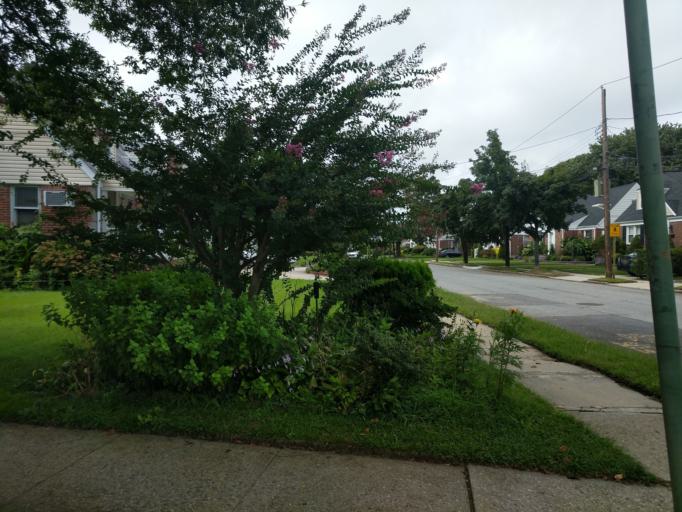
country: US
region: New York
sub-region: Nassau County
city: Malverne
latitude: 40.6800
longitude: -73.6729
